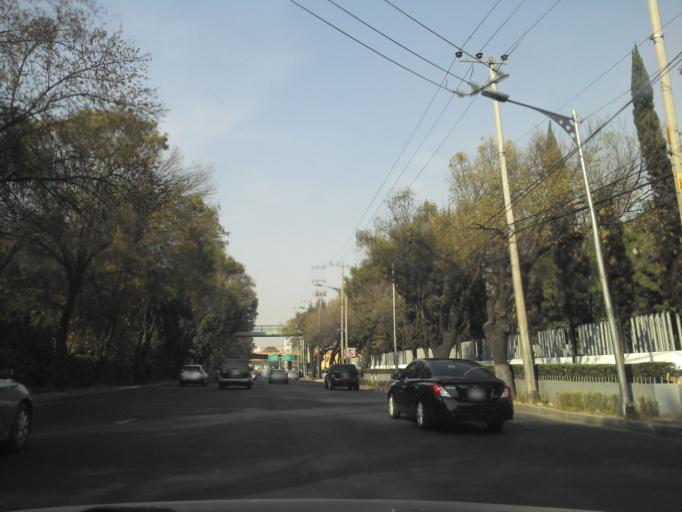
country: MX
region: Mexico City
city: Tlalpan
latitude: 19.3149
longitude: -99.1395
